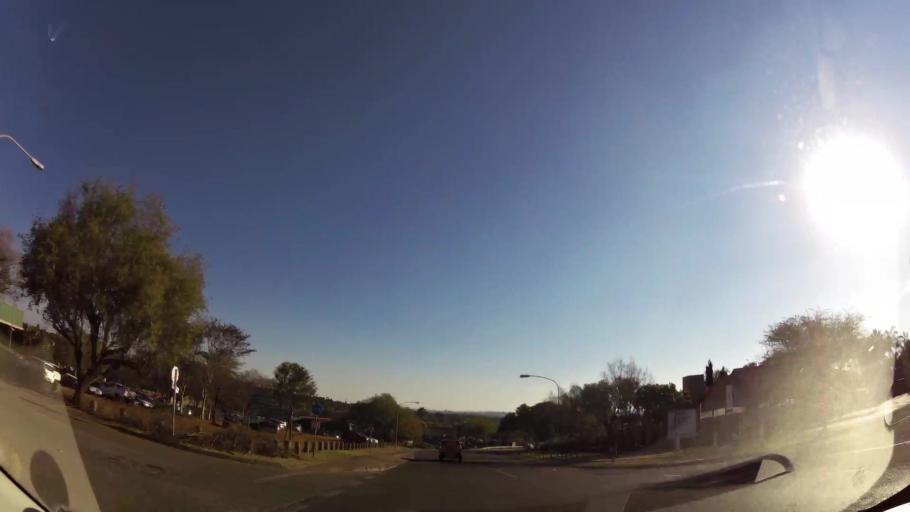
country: ZA
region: Gauteng
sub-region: City of Tshwane Metropolitan Municipality
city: Centurion
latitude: -25.8940
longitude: 28.1439
